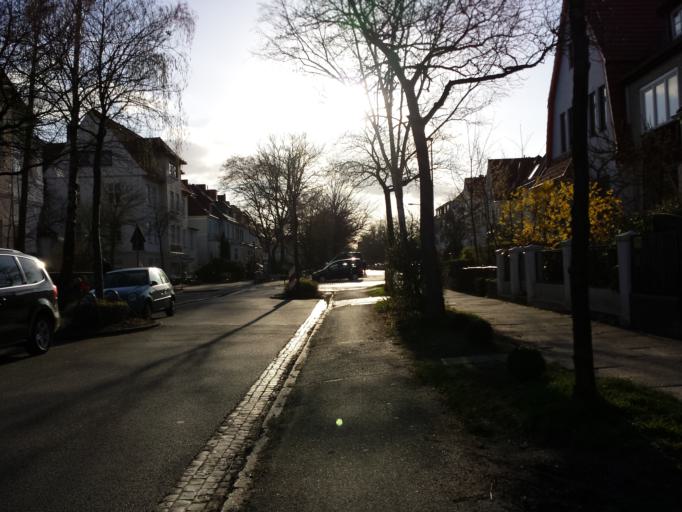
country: DE
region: Bremen
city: Bremen
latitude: 53.0857
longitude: 8.8406
